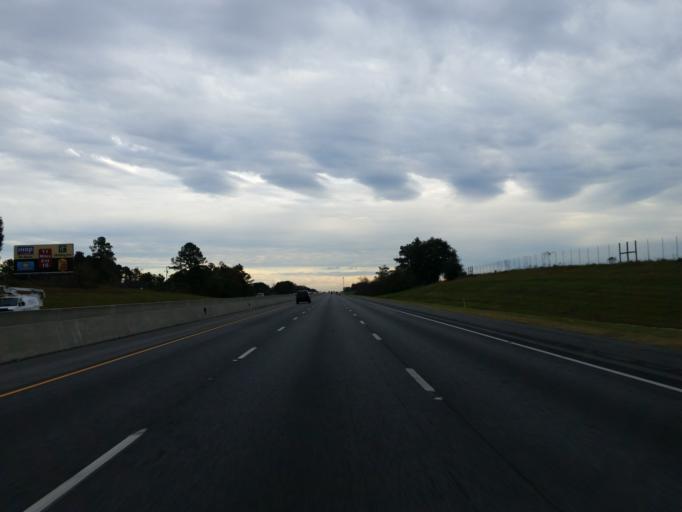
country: US
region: Georgia
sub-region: Lowndes County
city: Hahira
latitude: 30.9665
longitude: -83.3803
